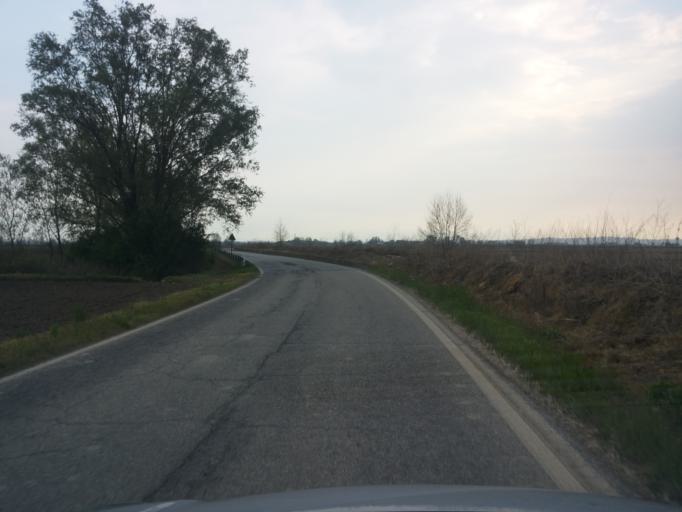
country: IT
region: Piedmont
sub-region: Provincia di Vercelli
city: Caresana
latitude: 45.2036
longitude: 8.4974
